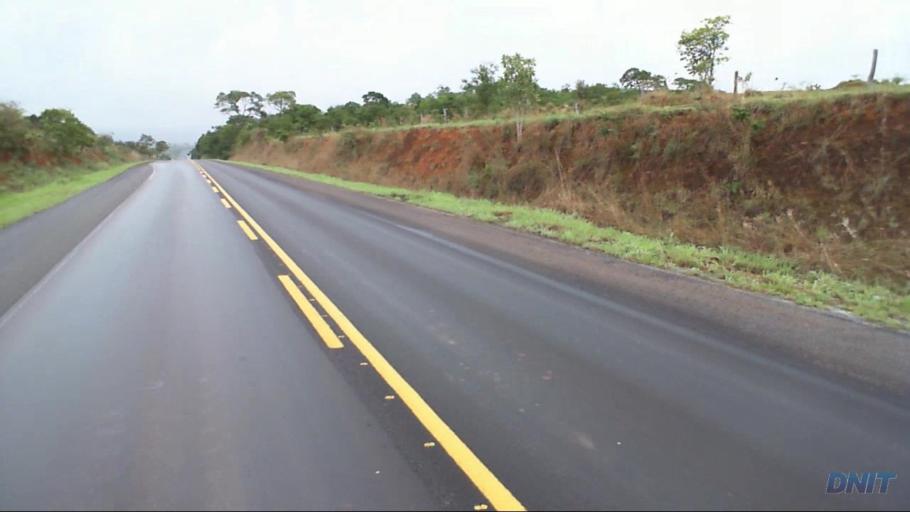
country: BR
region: Goias
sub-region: Padre Bernardo
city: Padre Bernardo
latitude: -15.2020
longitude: -48.4560
